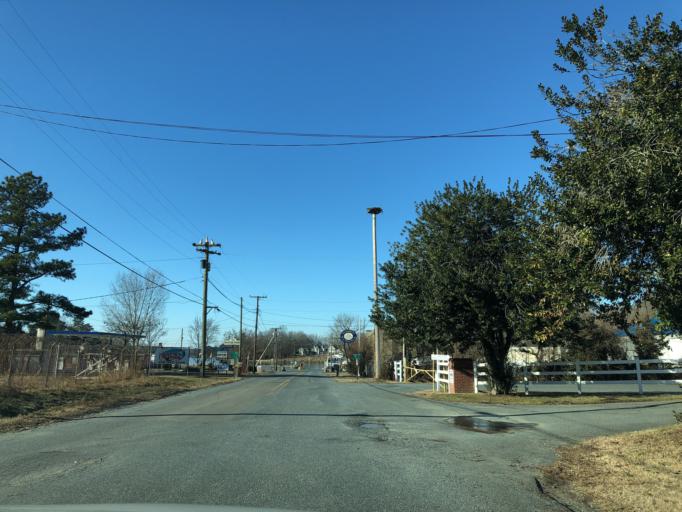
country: US
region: Maryland
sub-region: Talbot County
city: Easton
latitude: 38.7686
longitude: -76.0926
